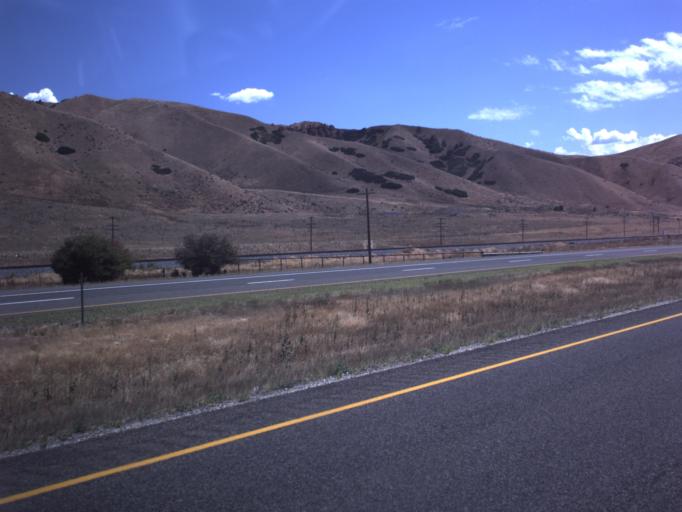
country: US
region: Utah
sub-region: Summit County
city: Coalville
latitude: 40.9894
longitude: -111.4551
